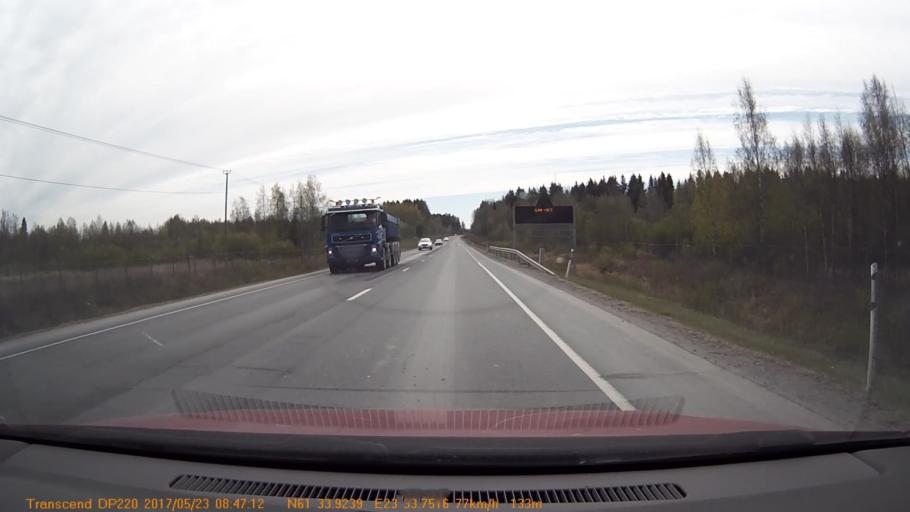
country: FI
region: Pirkanmaa
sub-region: Tampere
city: Yloejaervi
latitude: 61.5654
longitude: 23.5625
